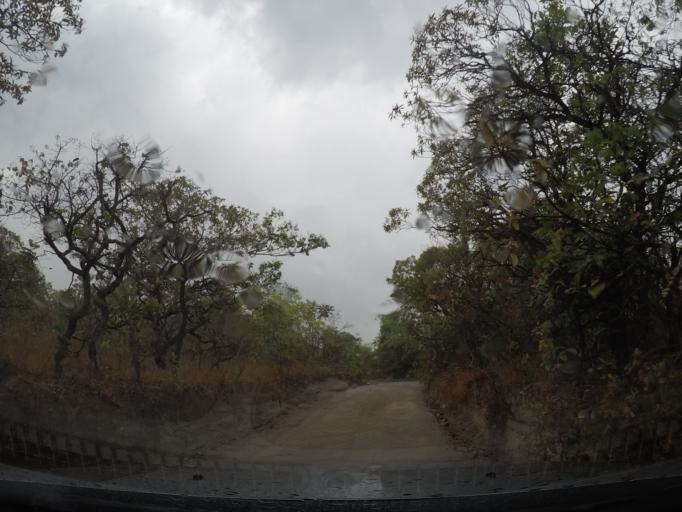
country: BR
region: Goias
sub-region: Pirenopolis
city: Pirenopolis
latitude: -15.8269
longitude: -48.8830
